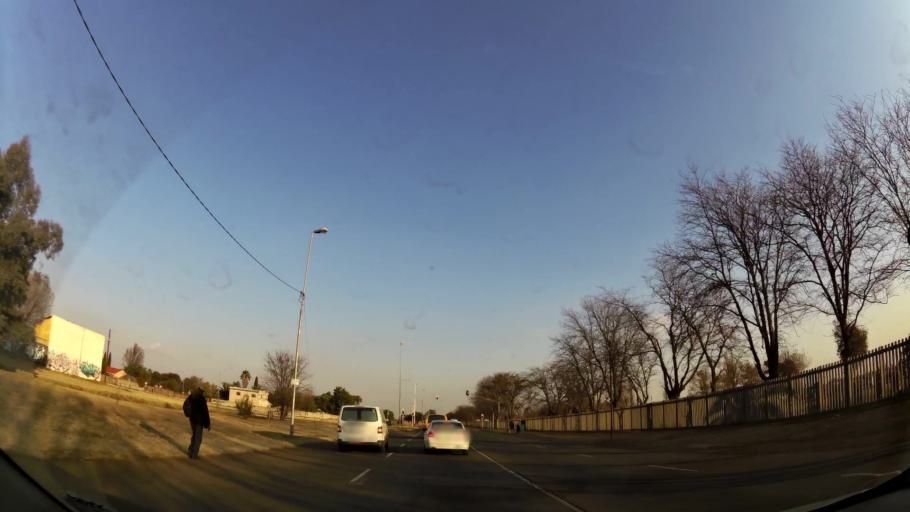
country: ZA
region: Gauteng
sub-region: Ekurhuleni Metropolitan Municipality
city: Germiston
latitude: -26.2780
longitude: 28.2262
